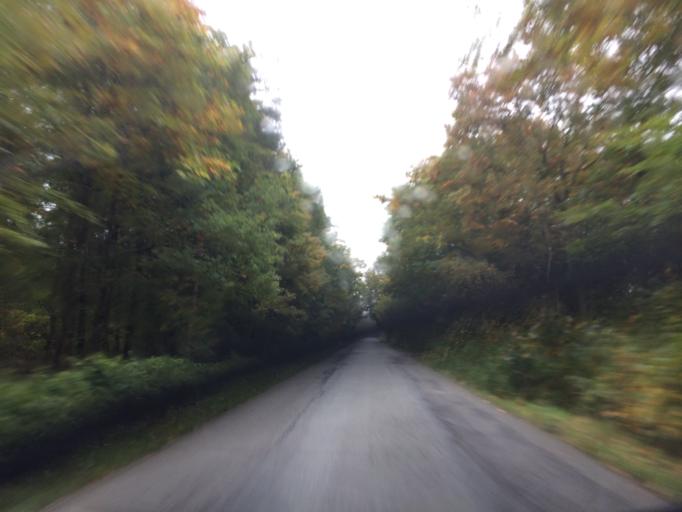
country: DK
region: Central Jutland
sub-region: Ringkobing-Skjern Kommune
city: Videbaek
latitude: 56.2077
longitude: 8.5446
